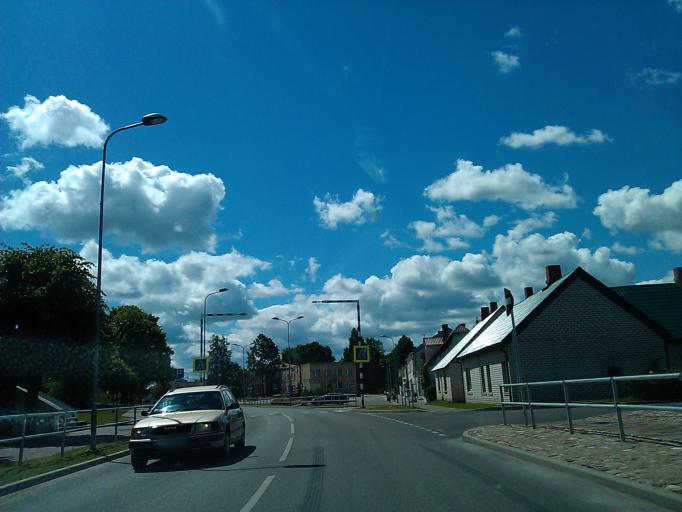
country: LV
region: Vilanu
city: Vilani
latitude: 56.5528
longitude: 26.9221
